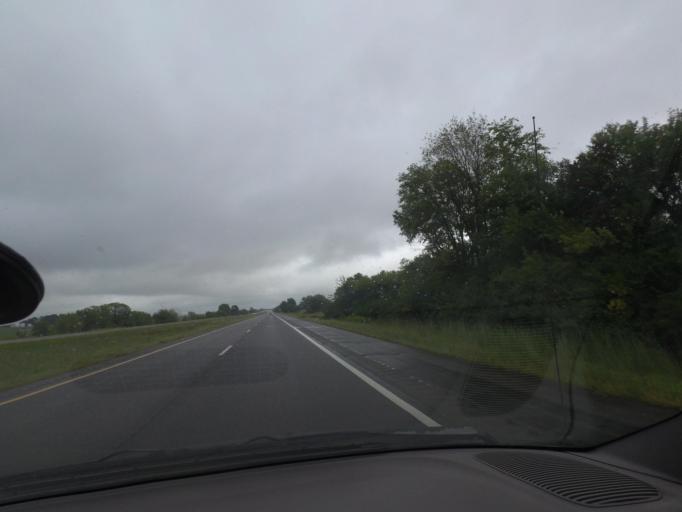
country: US
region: Illinois
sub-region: Champaign County
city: Mahomet
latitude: 40.1203
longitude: -88.4365
